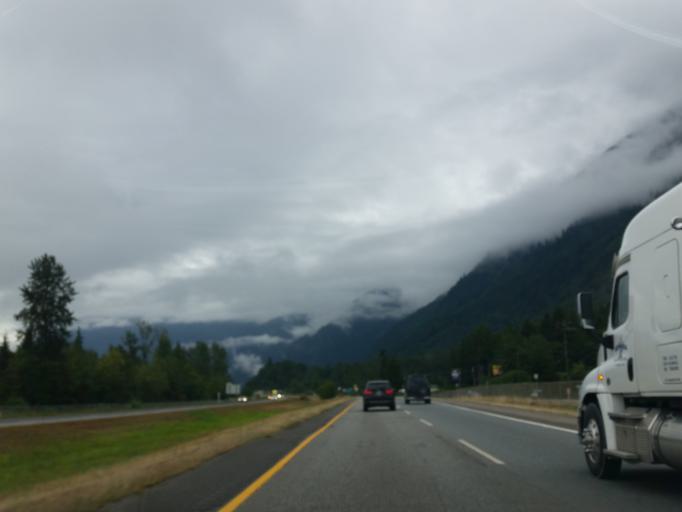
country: CA
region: British Columbia
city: Agassiz
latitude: 49.1862
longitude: -121.7486
